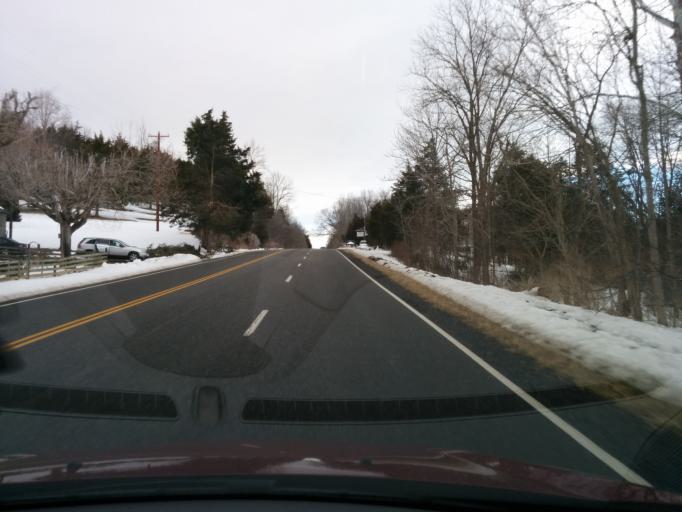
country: US
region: Virginia
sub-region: City of Lexington
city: Lexington
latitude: 37.7487
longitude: -79.4576
